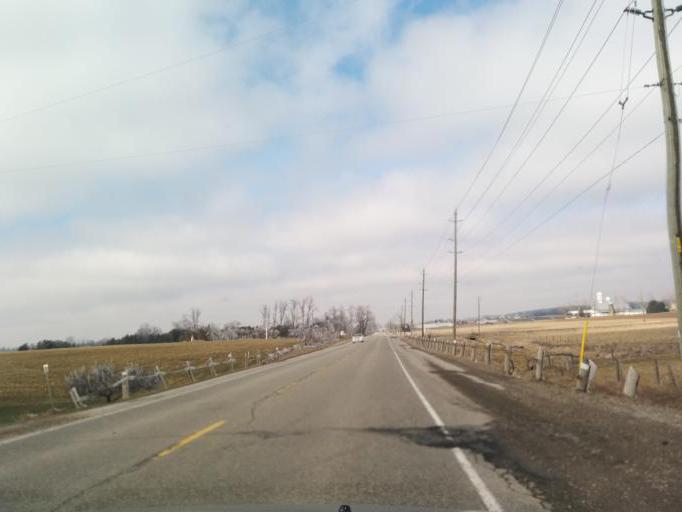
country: CA
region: Ontario
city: Waterloo
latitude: 43.6217
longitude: -80.5520
